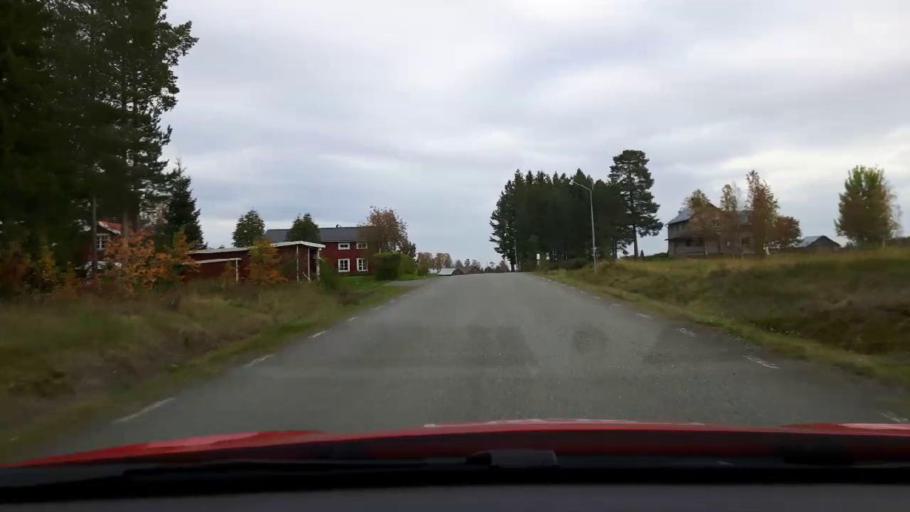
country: SE
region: Jaemtland
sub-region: Krokoms Kommun
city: Krokom
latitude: 63.2358
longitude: 14.1176
